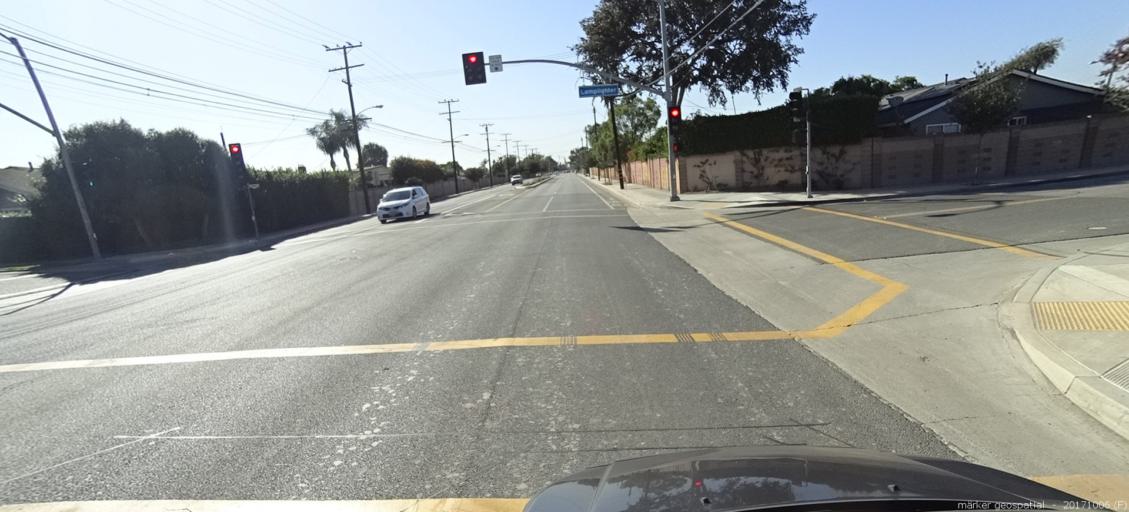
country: US
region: California
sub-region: Orange County
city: Westminster
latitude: 33.7811
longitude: -118.0160
